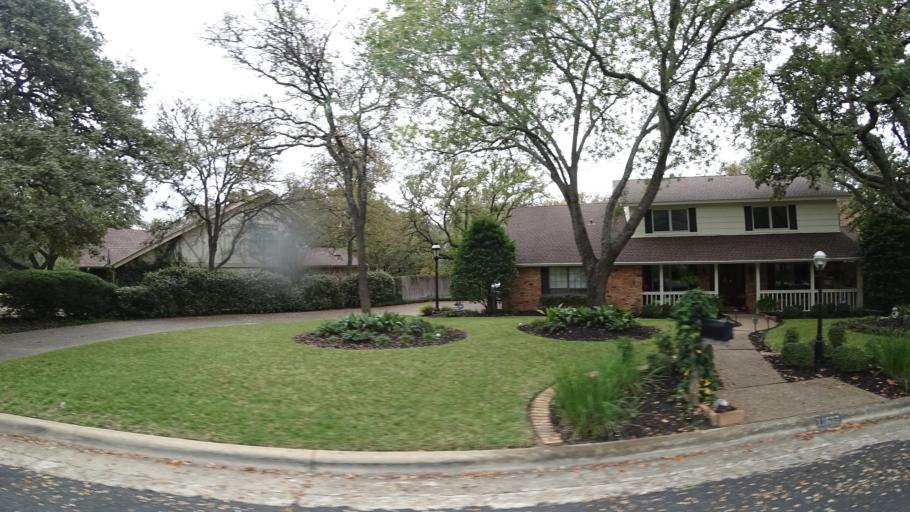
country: US
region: Texas
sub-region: Williamson County
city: Anderson Mill
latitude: 30.4434
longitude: -97.8128
